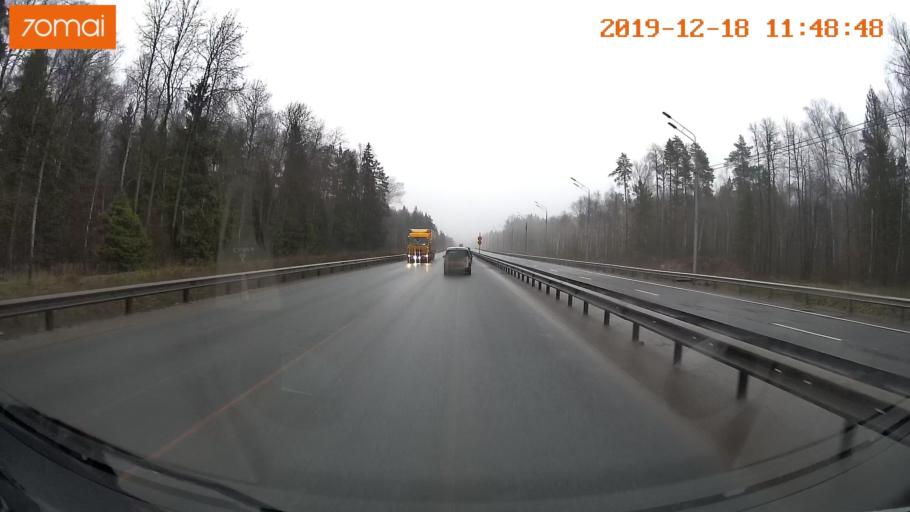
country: RU
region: Moskovskaya
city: Yershovo
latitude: 55.7717
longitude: 36.9065
